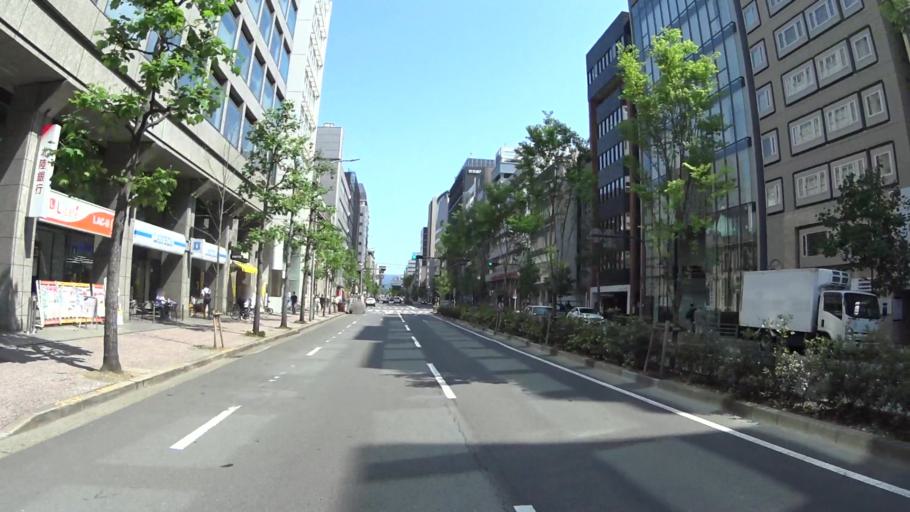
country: JP
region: Kyoto
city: Kyoto
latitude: 35.0052
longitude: 135.7597
